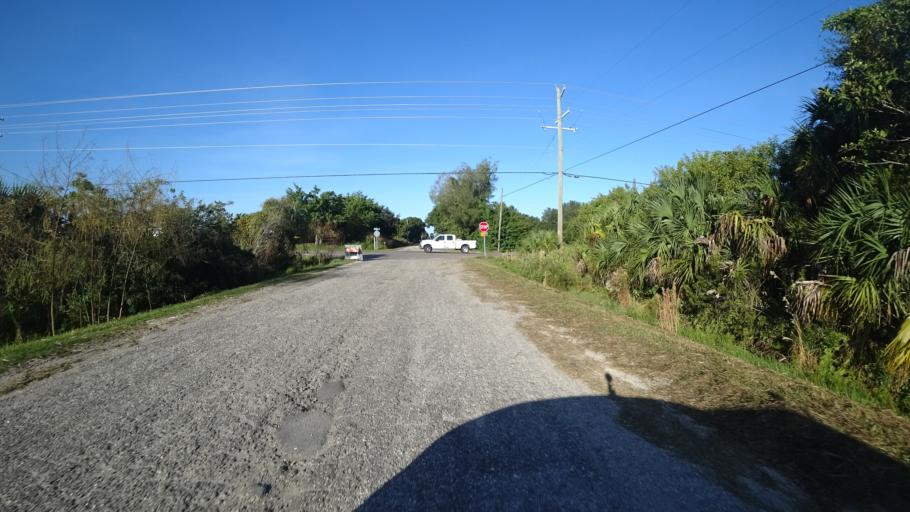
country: US
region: Florida
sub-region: Manatee County
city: Ellenton
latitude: 27.5682
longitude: -82.5274
